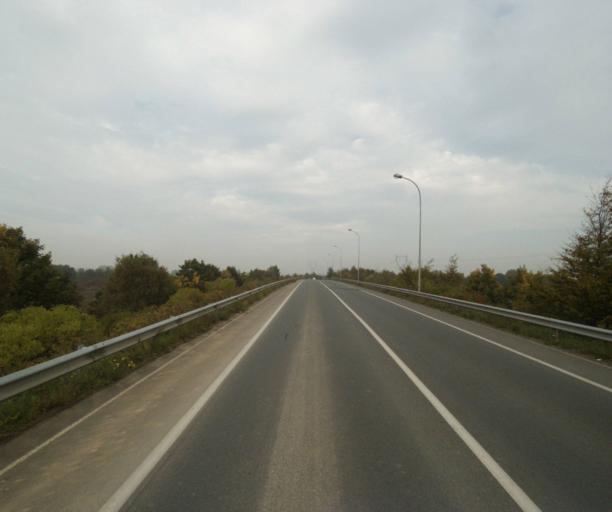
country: FR
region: Nord-Pas-de-Calais
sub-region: Departement du Nord
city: Phalempin
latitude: 50.5307
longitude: 3.0196
